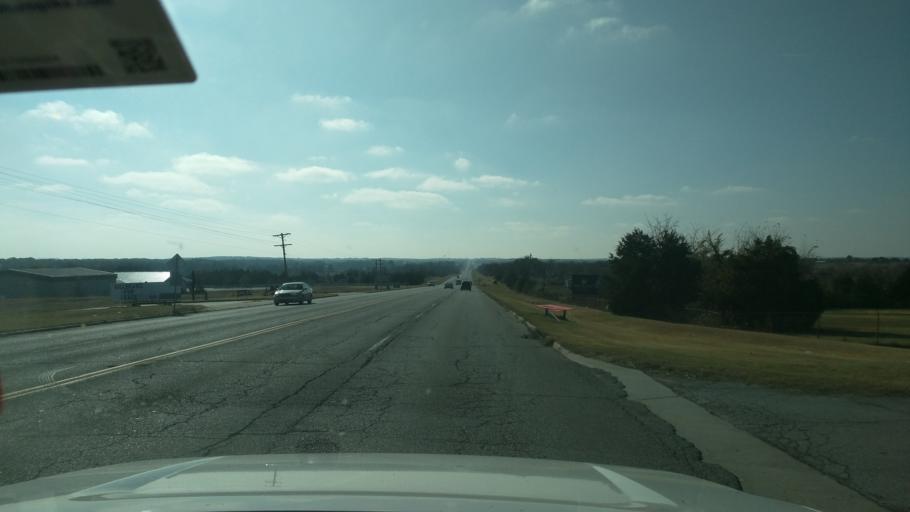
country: US
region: Oklahoma
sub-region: Washington County
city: Bartlesville
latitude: 36.6840
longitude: -95.9352
